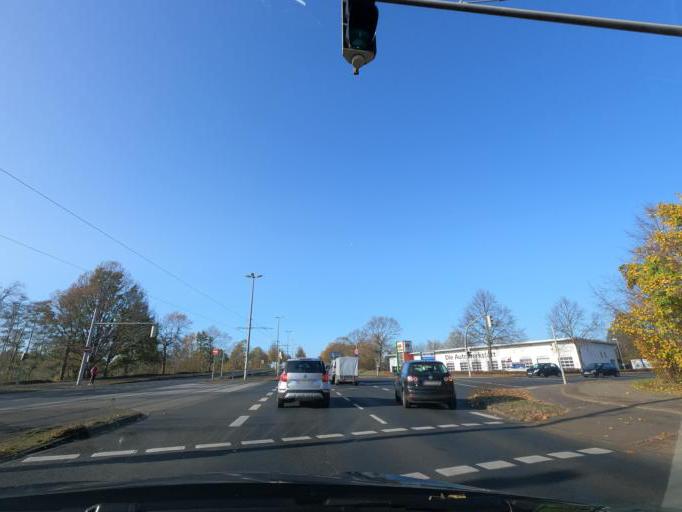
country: DE
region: Lower Saxony
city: Braunschweig
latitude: 52.2546
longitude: 10.5031
